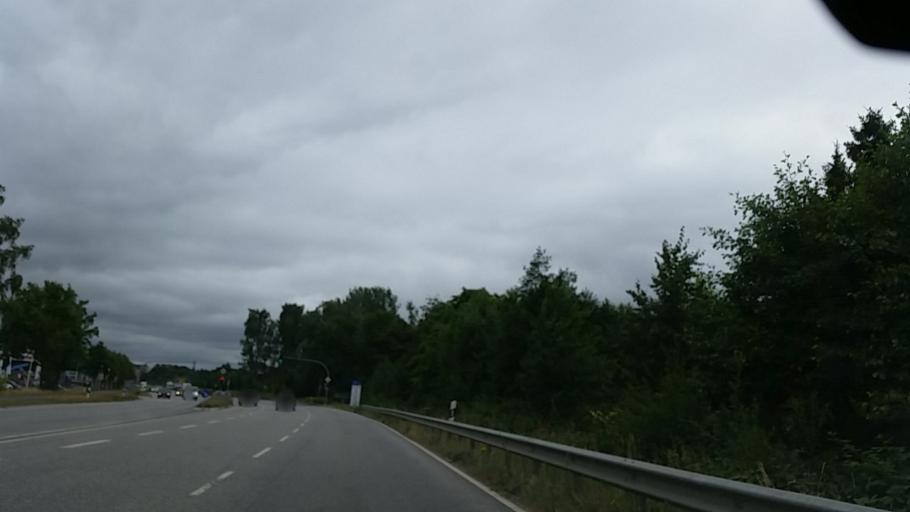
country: DE
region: Schleswig-Holstein
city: Windeby
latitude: 54.4733
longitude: 9.8251
